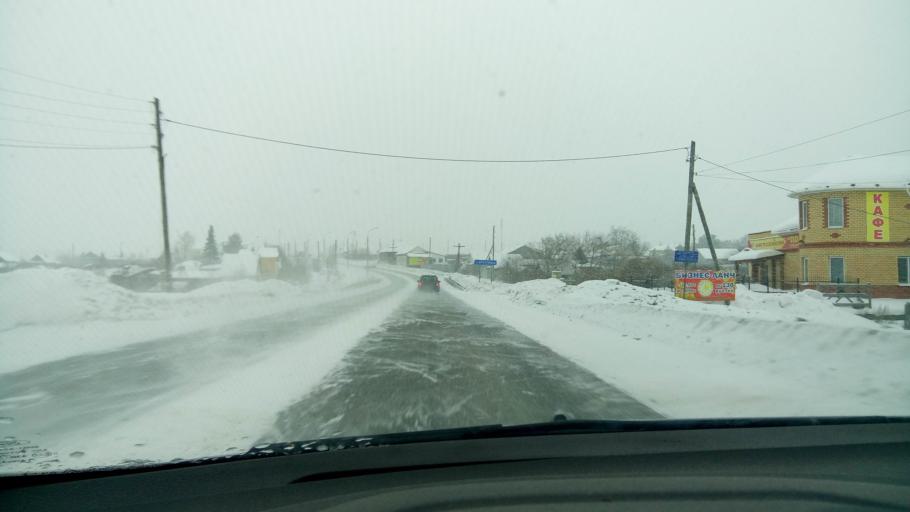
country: RU
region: Sverdlovsk
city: Verkhneye Dubrovo
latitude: 56.7357
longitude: 61.1255
